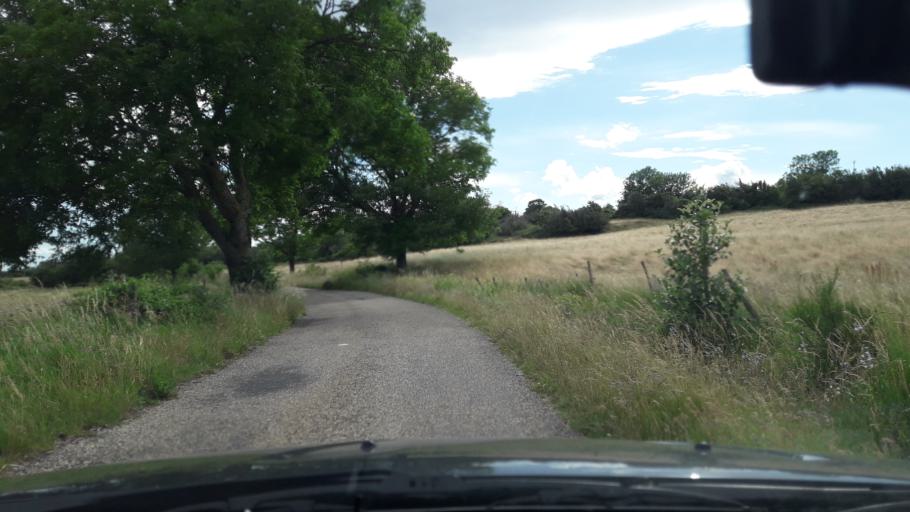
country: FR
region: Rhone-Alpes
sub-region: Departement de l'Ardeche
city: Saint-Priest
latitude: 44.6726
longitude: 4.5661
